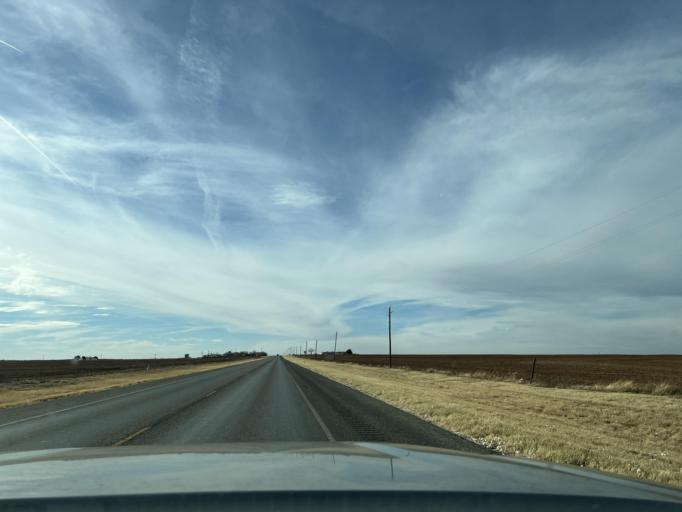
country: US
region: Texas
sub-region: Jones County
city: Anson
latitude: 32.7517
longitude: -99.9095
